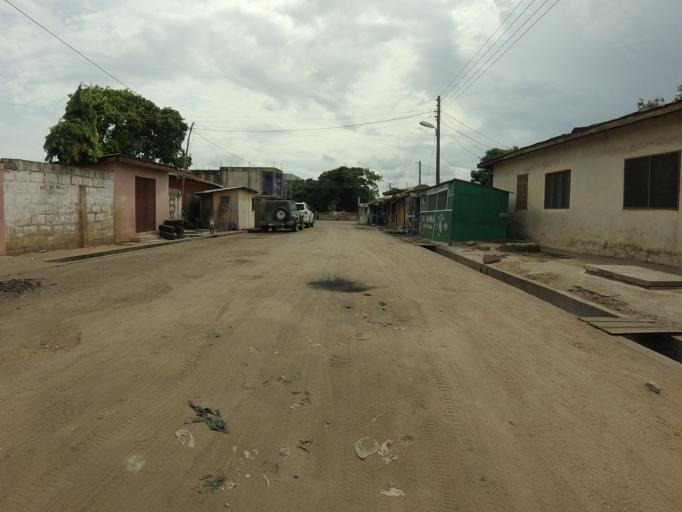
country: GH
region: Greater Accra
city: Accra
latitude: 5.5952
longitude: -0.2163
